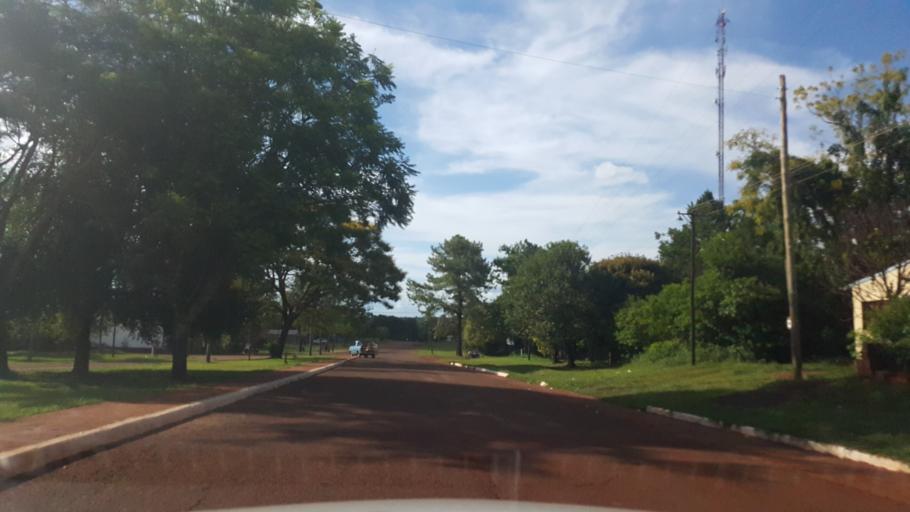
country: AR
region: Misiones
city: Santa Ana
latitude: -27.3679
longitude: -55.5825
